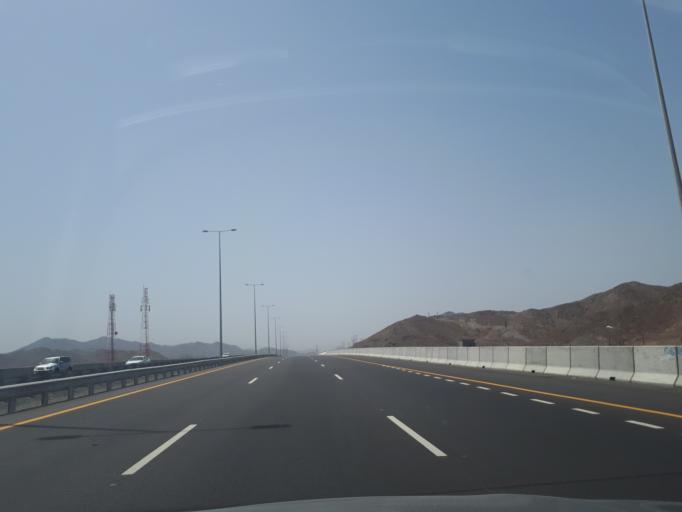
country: OM
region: Muhafazat ad Dakhiliyah
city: Bidbid
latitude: 23.3944
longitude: 58.0996
